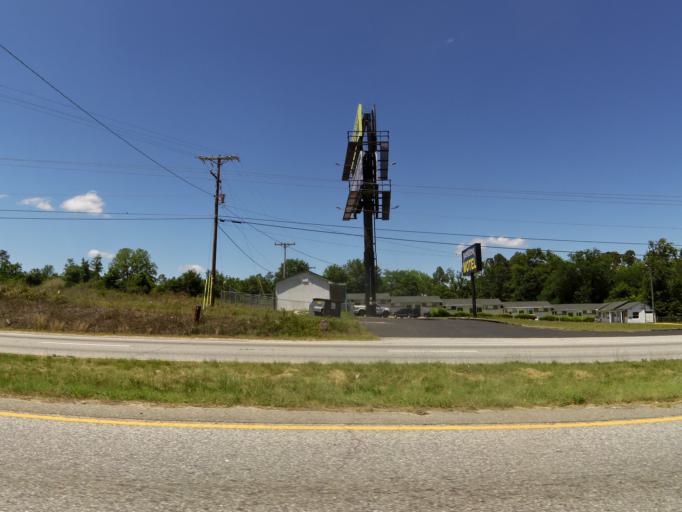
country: US
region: South Carolina
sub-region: Aiken County
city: Clearwater
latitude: 33.5034
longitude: -81.9021
